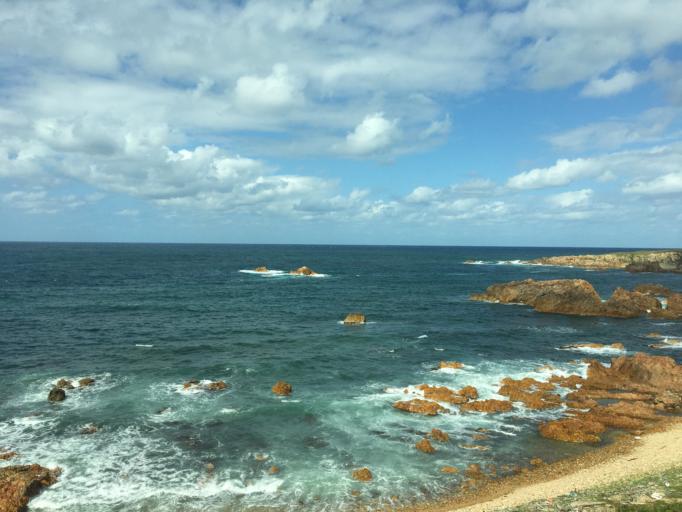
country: JP
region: Aomori
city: Shimokizukuri
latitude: 40.6643
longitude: 139.9390
